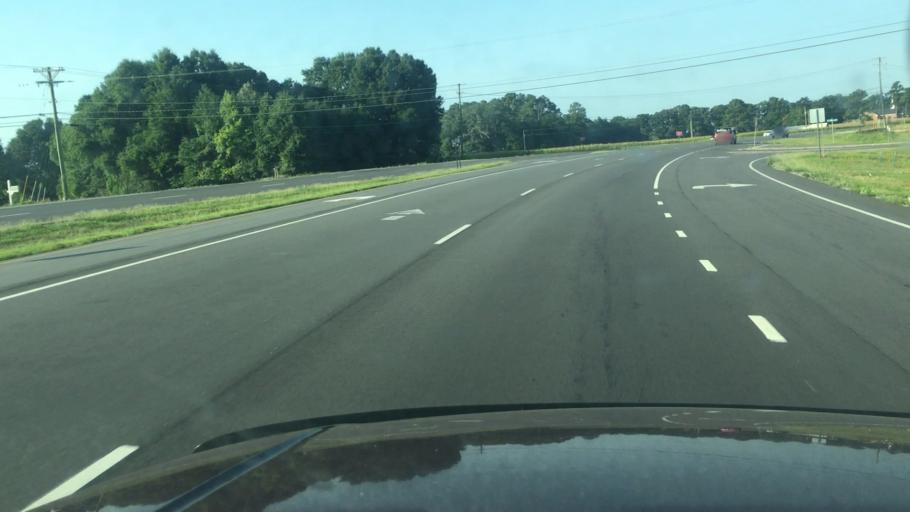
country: US
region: North Carolina
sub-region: Cumberland County
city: Hope Mills
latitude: 34.9368
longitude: -78.8476
